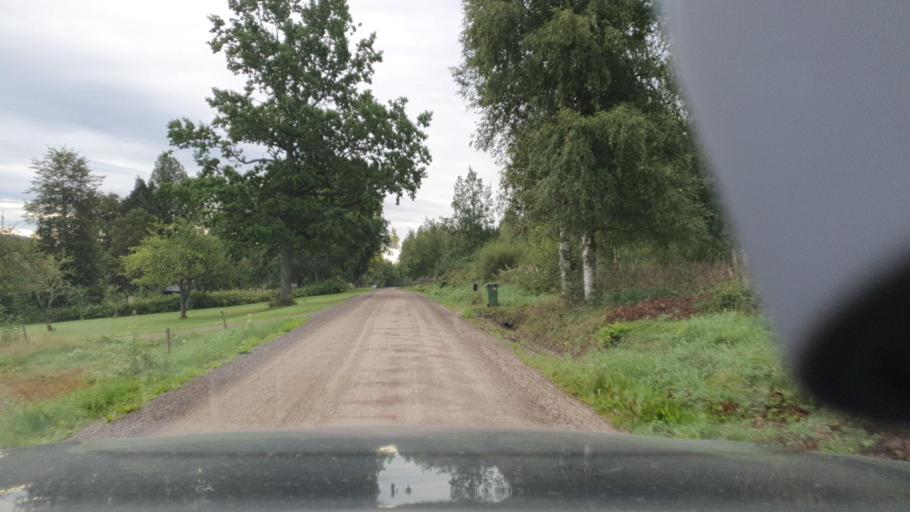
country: SE
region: Vaermland
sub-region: Torsby Kommun
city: Torsby
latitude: 59.9654
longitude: 12.8781
